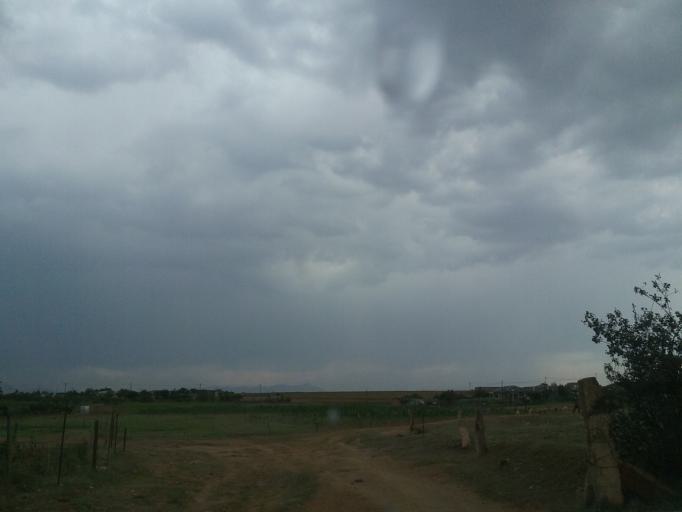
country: LS
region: Maseru
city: Maseru
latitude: -29.4219
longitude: 27.5691
